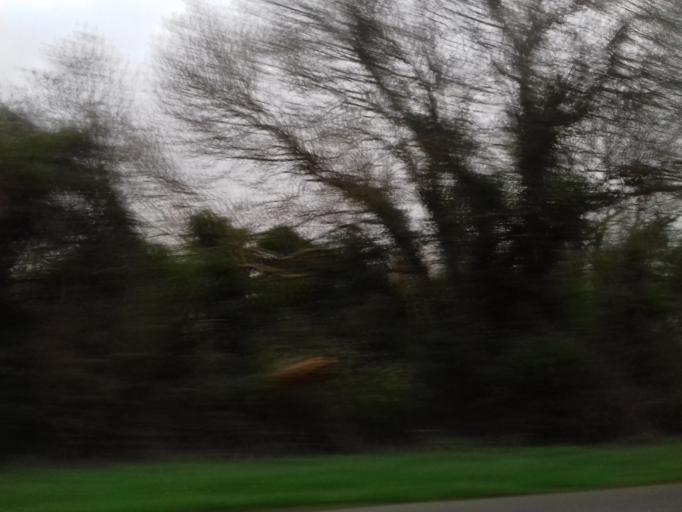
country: IE
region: Munster
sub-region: County Limerick
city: Rathkeale
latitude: 52.4922
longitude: -9.0004
